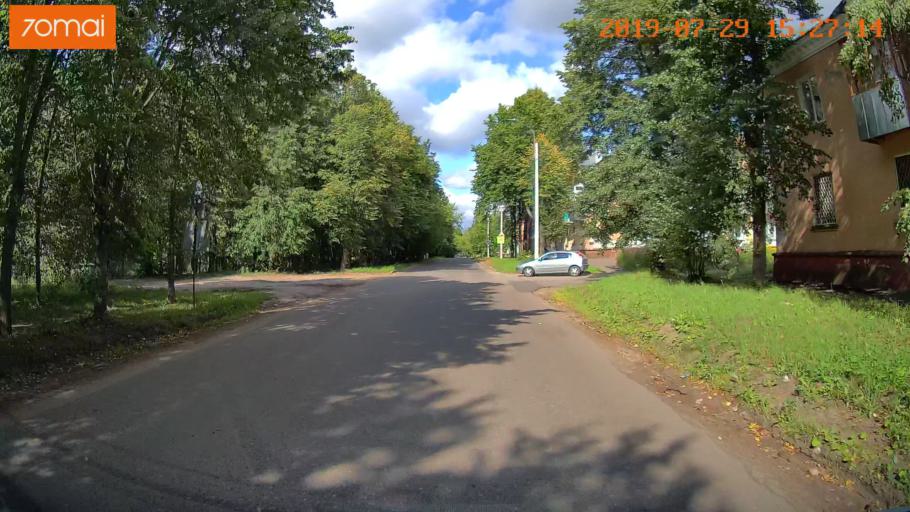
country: RU
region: Ivanovo
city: Bogorodskoye
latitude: 57.0212
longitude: 41.0065
